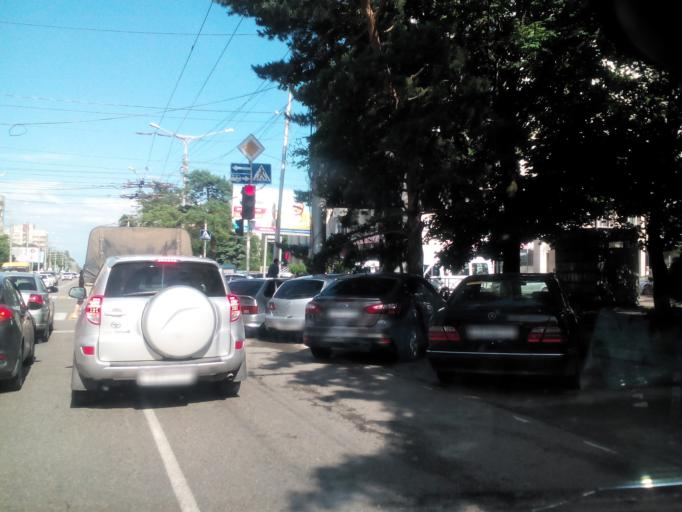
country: RU
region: Stavropol'skiy
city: Stavropol'
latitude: 45.0371
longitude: 41.9657
